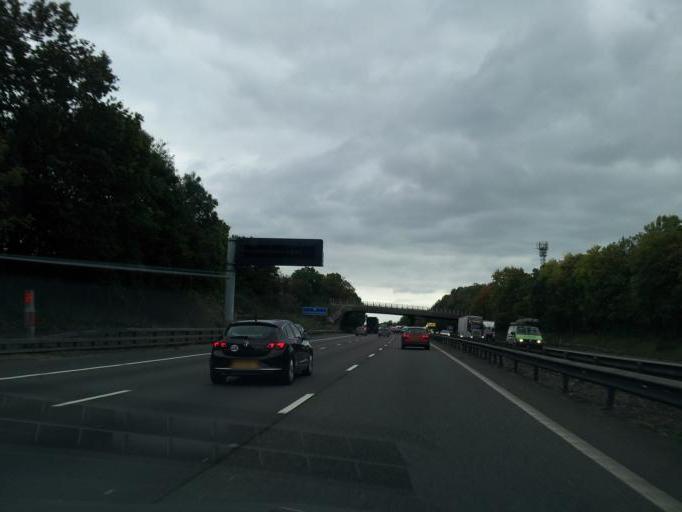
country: GB
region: England
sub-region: Milton Keynes
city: Hanslope
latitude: 52.1360
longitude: -0.8300
